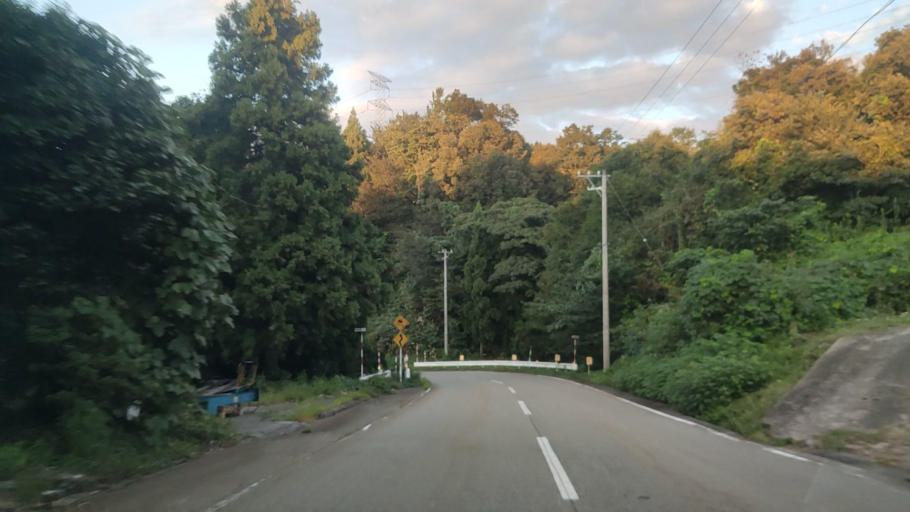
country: JP
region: Ishikawa
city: Tsubata
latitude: 36.6217
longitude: 136.7803
